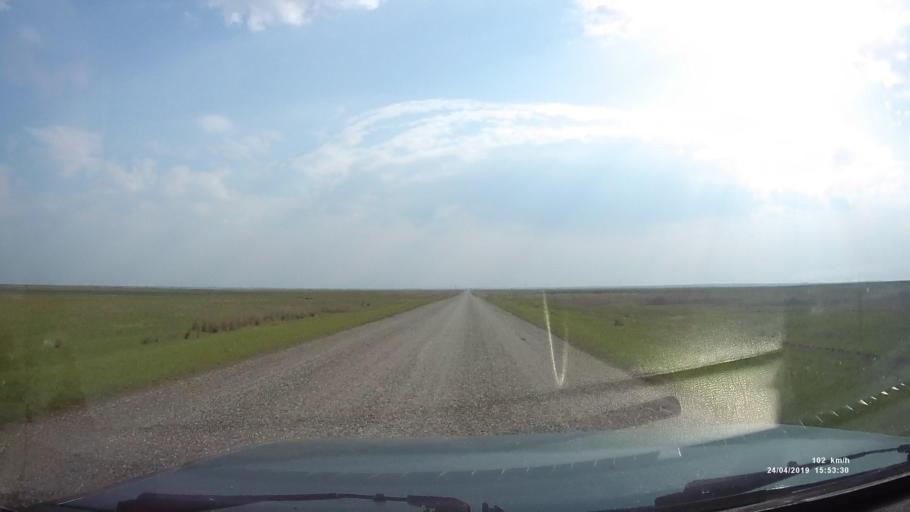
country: RU
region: Kalmykiya
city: Yashalta
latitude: 46.5975
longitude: 42.5750
